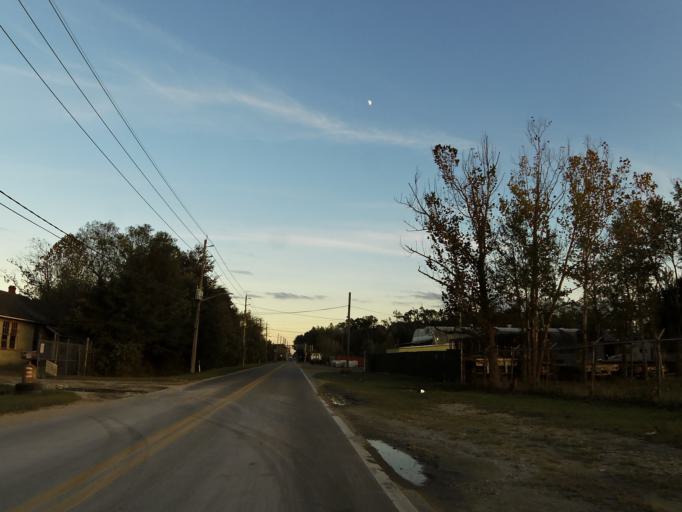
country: US
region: Florida
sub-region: Duval County
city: Jacksonville
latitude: 30.3594
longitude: -81.7243
